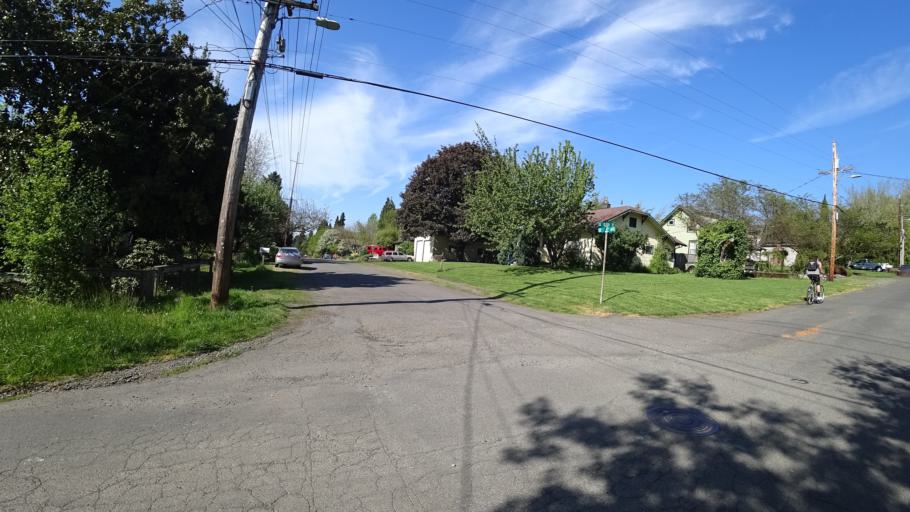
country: US
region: Oregon
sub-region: Clackamas County
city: Milwaukie
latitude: 45.4546
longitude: -122.6327
